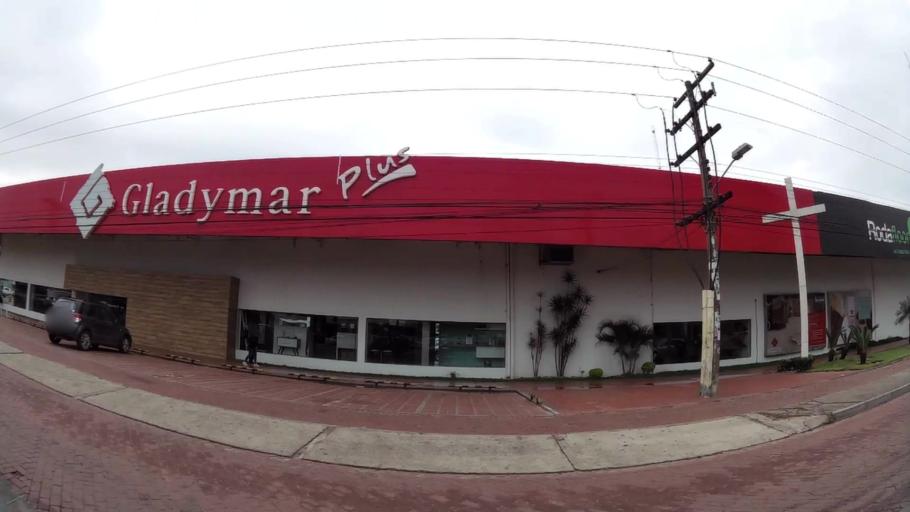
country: BO
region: Santa Cruz
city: Santa Cruz de la Sierra
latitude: -17.7606
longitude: -63.1794
